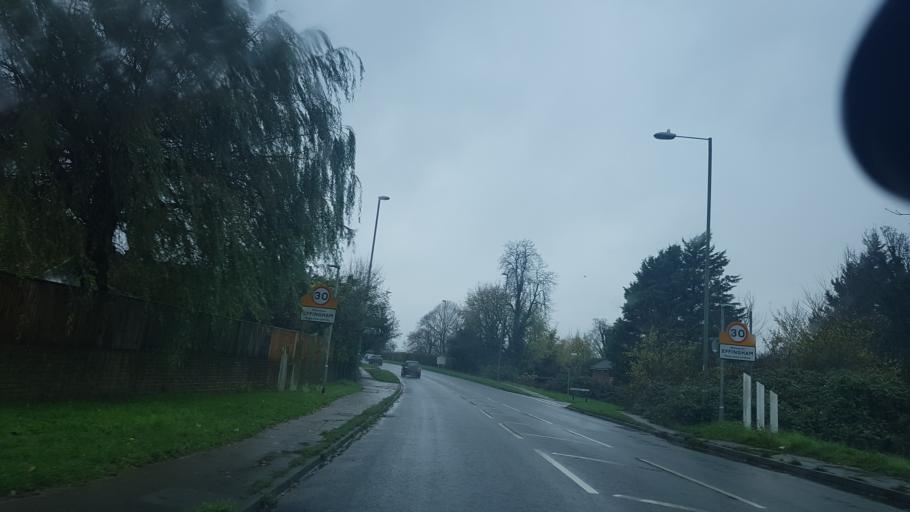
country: GB
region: England
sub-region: Surrey
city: Great Bookham
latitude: 51.2696
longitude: -0.3894
